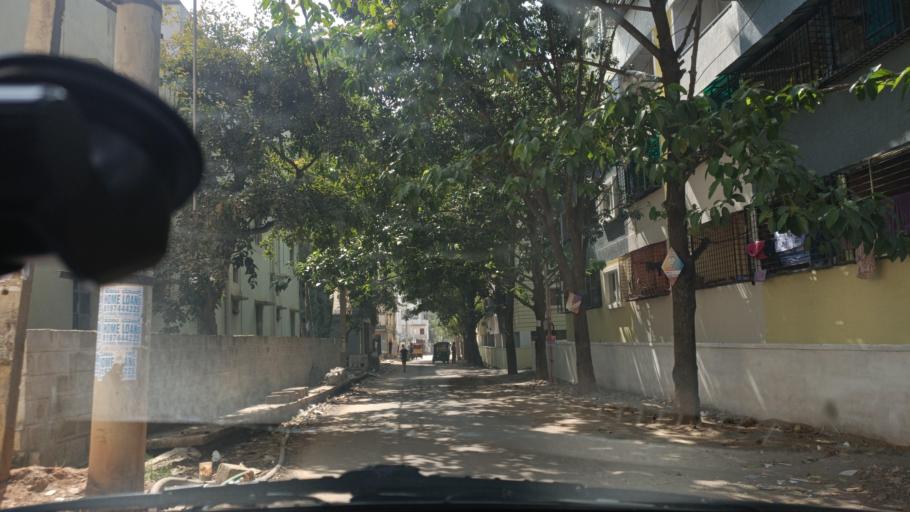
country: IN
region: Karnataka
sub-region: Bangalore Urban
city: Yelahanka
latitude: 13.1191
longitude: 77.6178
